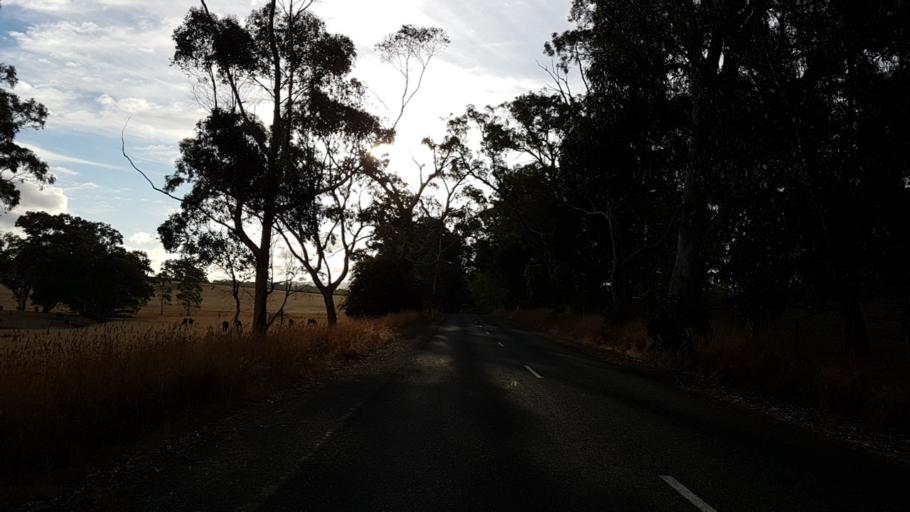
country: AU
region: South Australia
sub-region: Adelaide Hills
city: Woodside
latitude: -34.9792
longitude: 138.8867
